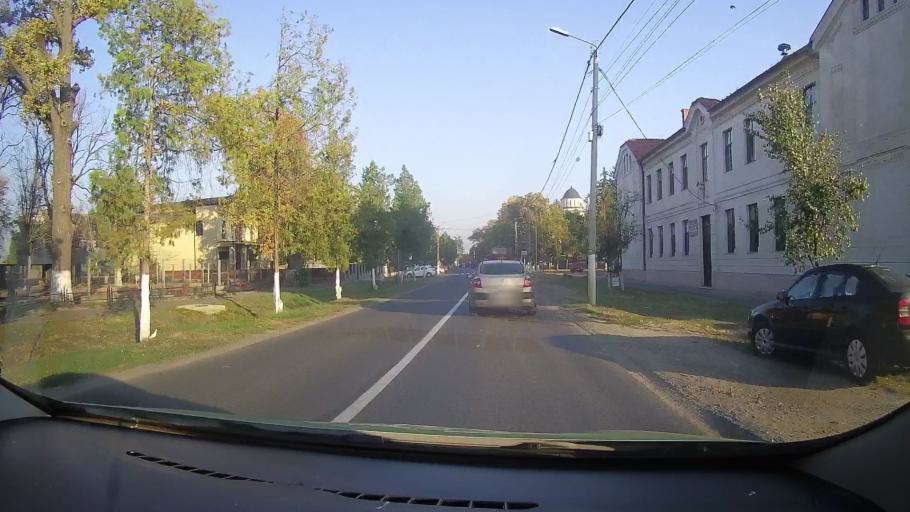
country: RO
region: Arad
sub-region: Comuna Curtici
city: Curtici
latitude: 46.3401
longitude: 21.3084
